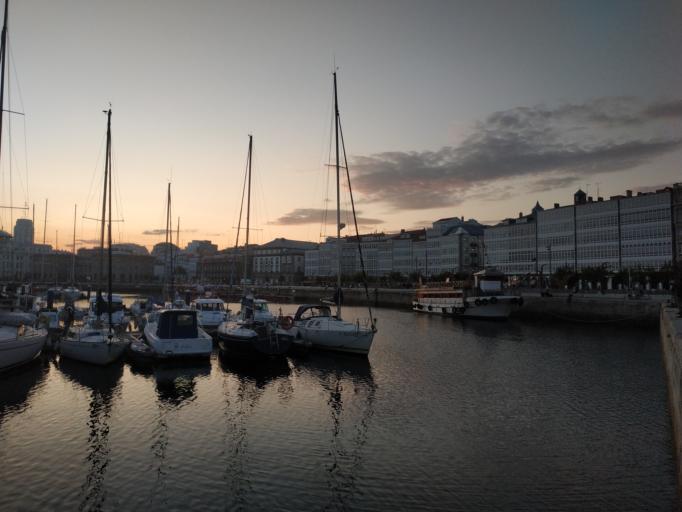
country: ES
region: Galicia
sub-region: Provincia da Coruna
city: A Coruna
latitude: 43.3691
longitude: -8.3956
